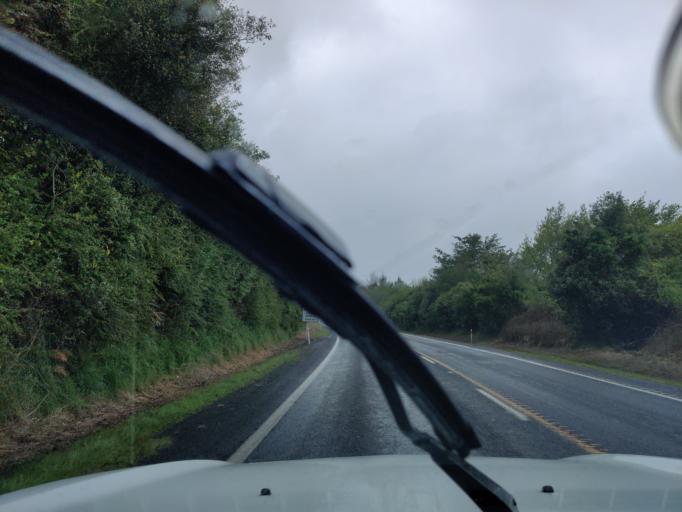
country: NZ
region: Bay of Plenty
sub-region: Rotorua District
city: Rotorua
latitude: -38.0779
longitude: 176.1835
